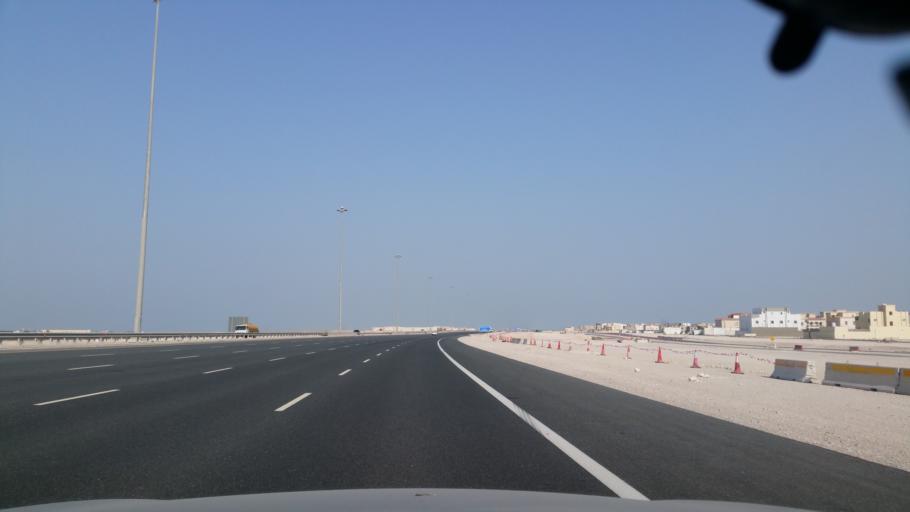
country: QA
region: Baladiyat Umm Salal
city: Umm Salal `Ali
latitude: 25.4564
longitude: 51.4431
